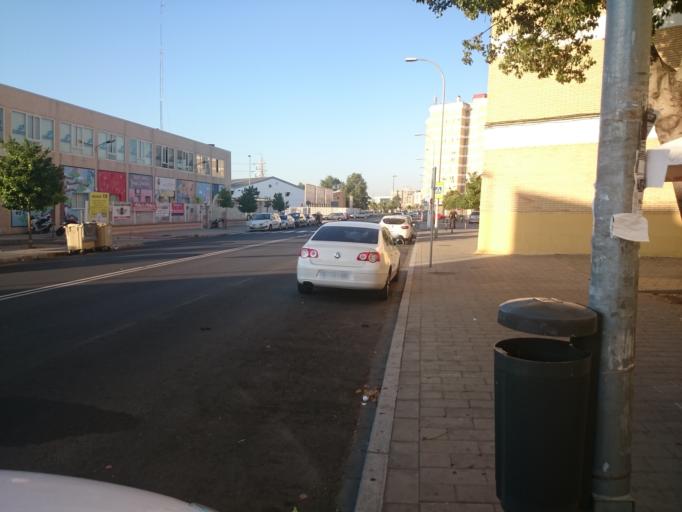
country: ES
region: Andalusia
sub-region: Provincia de Sevilla
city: Sevilla
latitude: 37.3930
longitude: -5.9580
